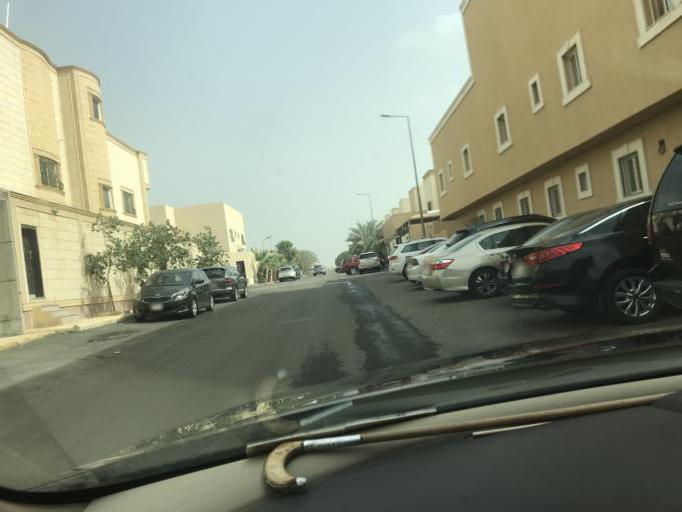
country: SA
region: Ar Riyad
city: Riyadh
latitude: 24.7996
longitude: 46.6666
